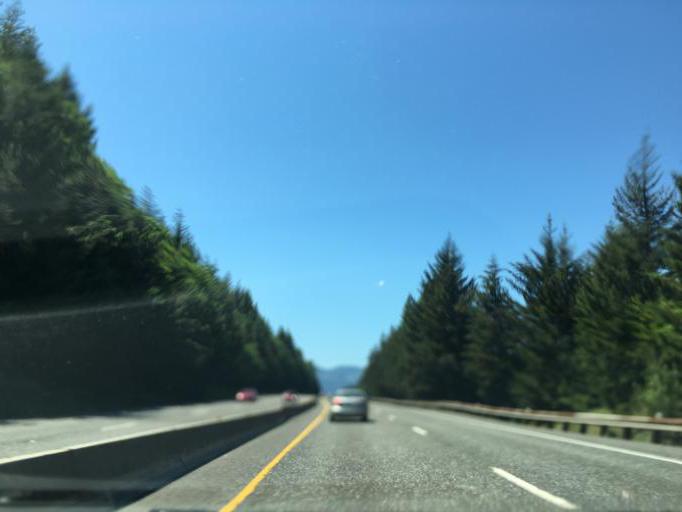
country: US
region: Washington
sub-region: Skamania County
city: Carson
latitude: 45.6966
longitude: -121.8025
